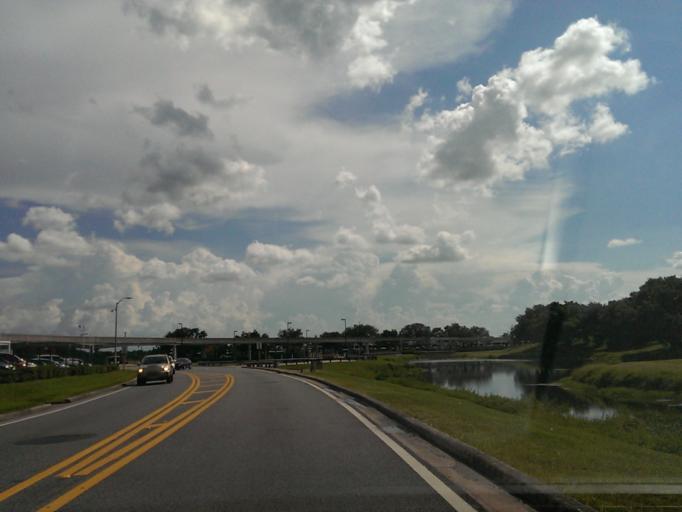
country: US
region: Florida
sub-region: Orange County
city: Bay Hill
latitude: 28.4188
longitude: -81.5765
